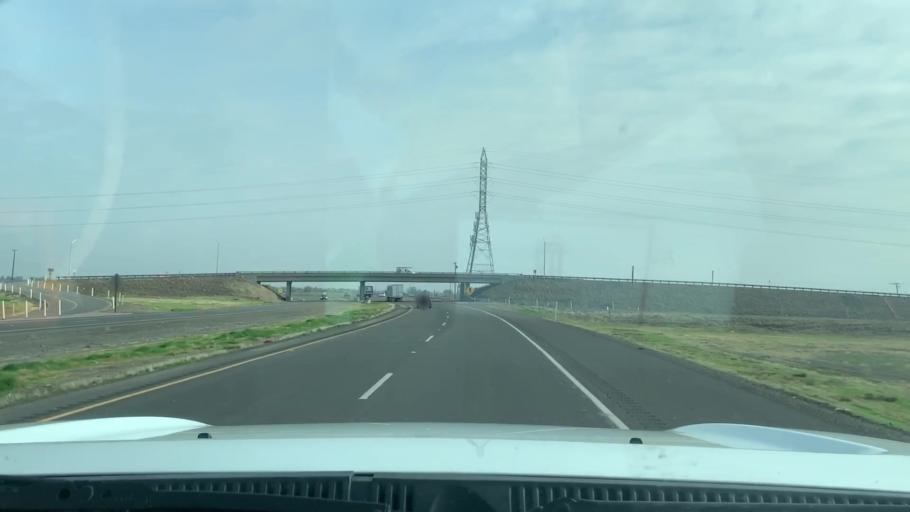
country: US
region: California
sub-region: Kings County
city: Lemoore Station
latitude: 36.2554
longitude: -119.8715
